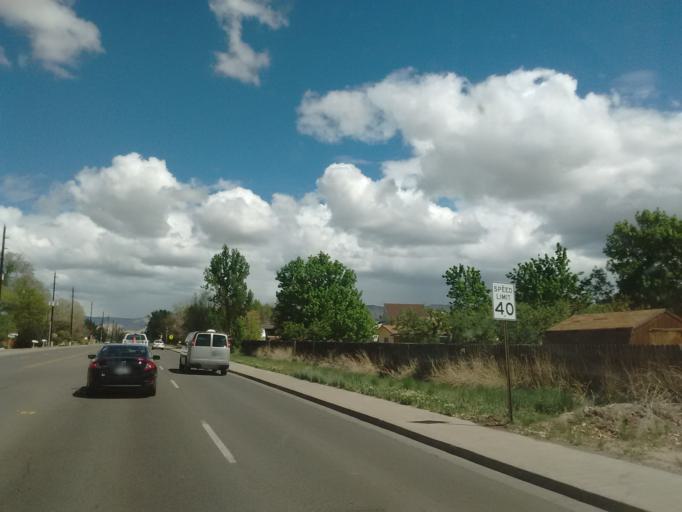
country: US
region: Colorado
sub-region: Mesa County
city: Fruitvale
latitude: 39.0852
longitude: -108.4965
